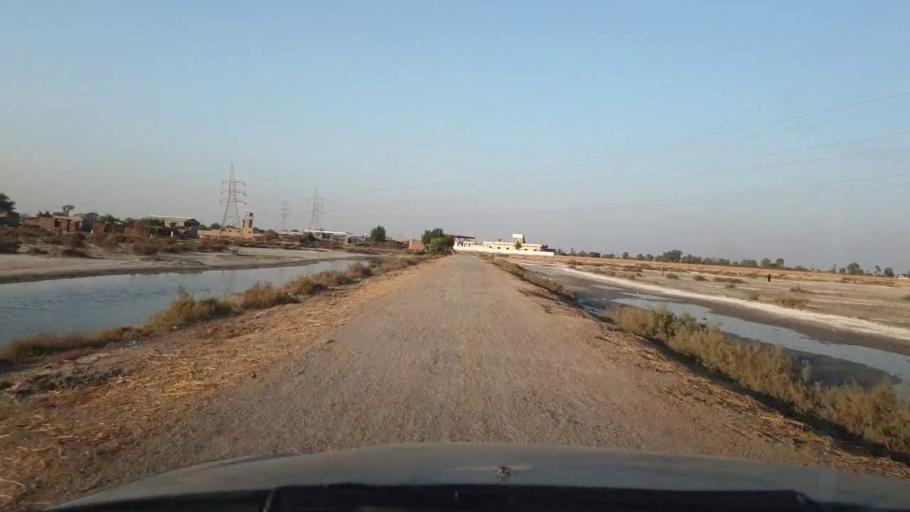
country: PK
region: Sindh
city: Matli
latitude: 25.0412
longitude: 68.6339
